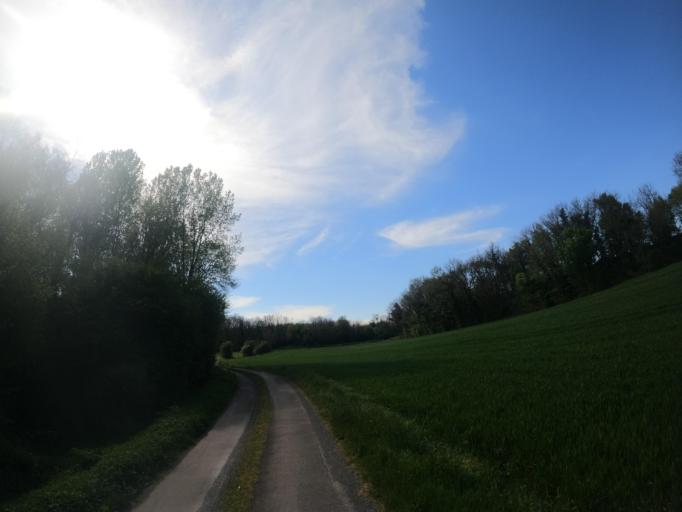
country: FR
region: Poitou-Charentes
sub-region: Departement des Deux-Sevres
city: Saint-Varent
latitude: 46.9163
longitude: -0.2018
